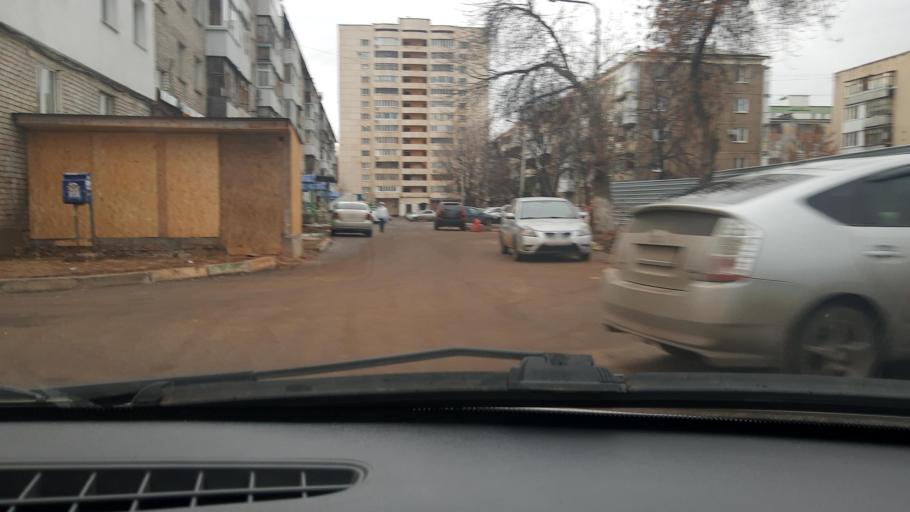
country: RU
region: Bashkortostan
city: Mikhaylovka
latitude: 54.7035
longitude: 55.8336
